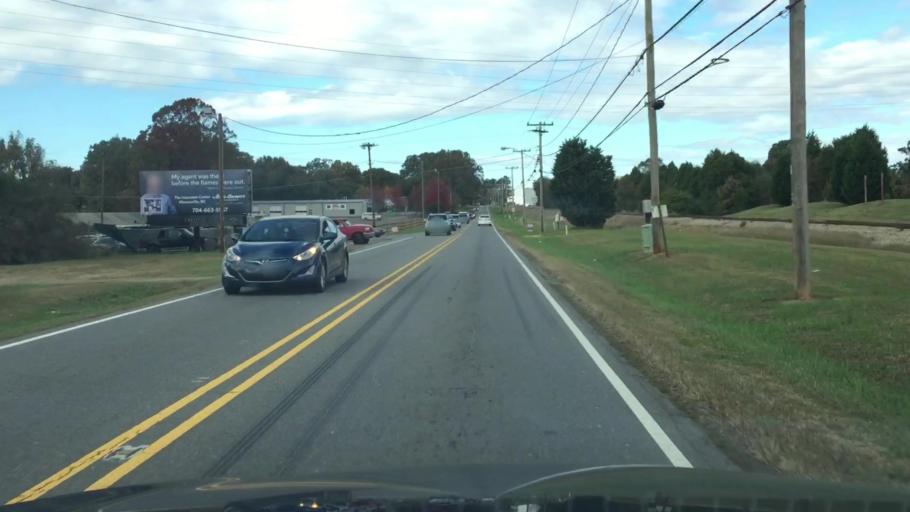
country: US
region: North Carolina
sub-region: Iredell County
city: Mooresville
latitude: 35.6076
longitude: -80.8161
